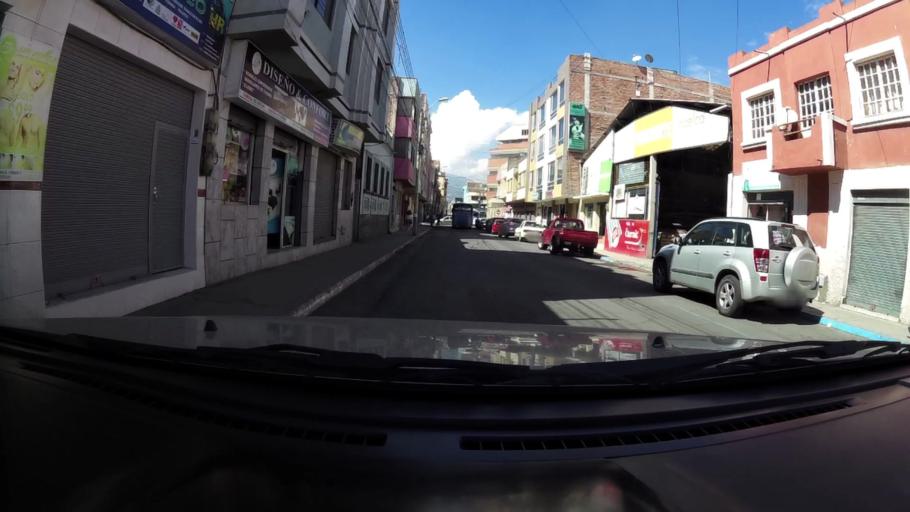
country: EC
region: Chimborazo
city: Riobamba
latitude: -1.6682
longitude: -78.6519
